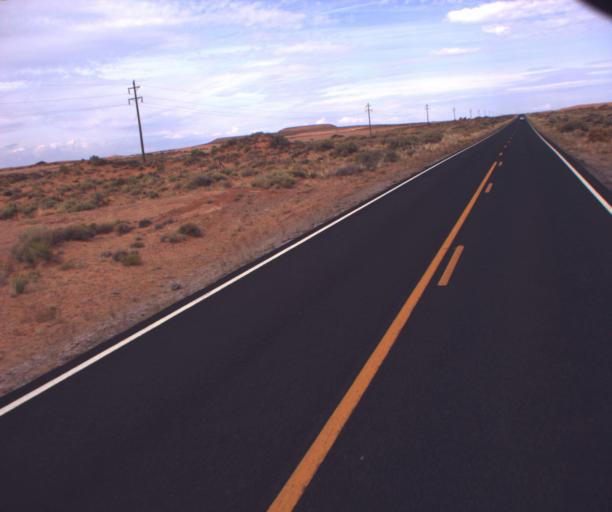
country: US
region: Arizona
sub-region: Apache County
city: Many Farms
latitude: 36.8155
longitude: -109.6462
